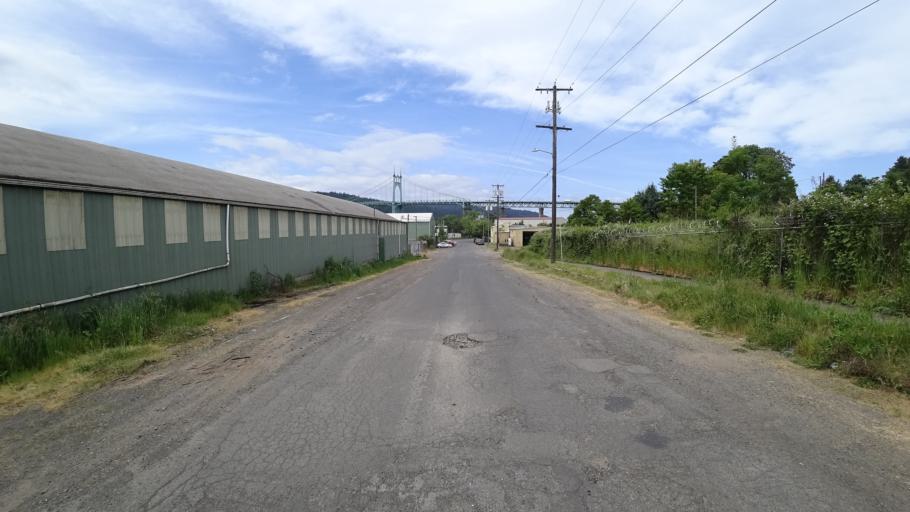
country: US
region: Oregon
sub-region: Washington County
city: West Haven
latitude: 45.5848
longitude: -122.7552
